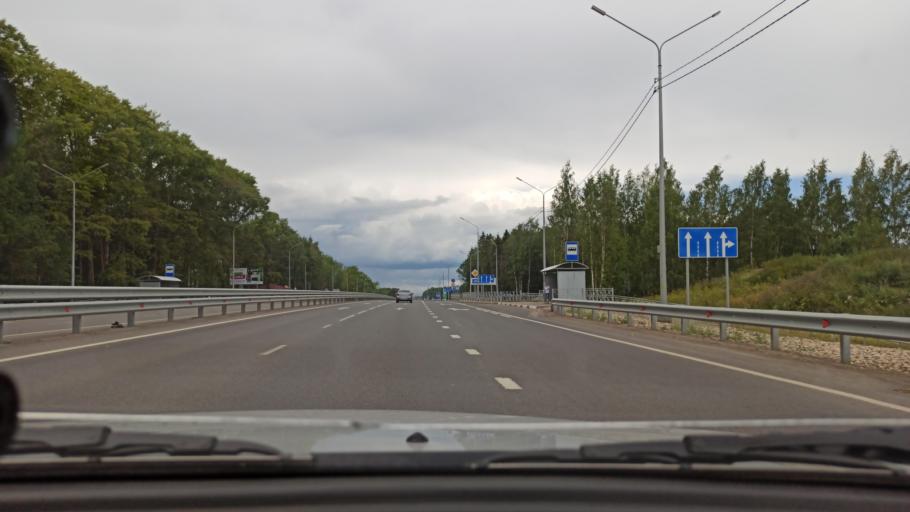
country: RU
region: Vologda
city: Molochnoye
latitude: 59.2593
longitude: 39.7516
